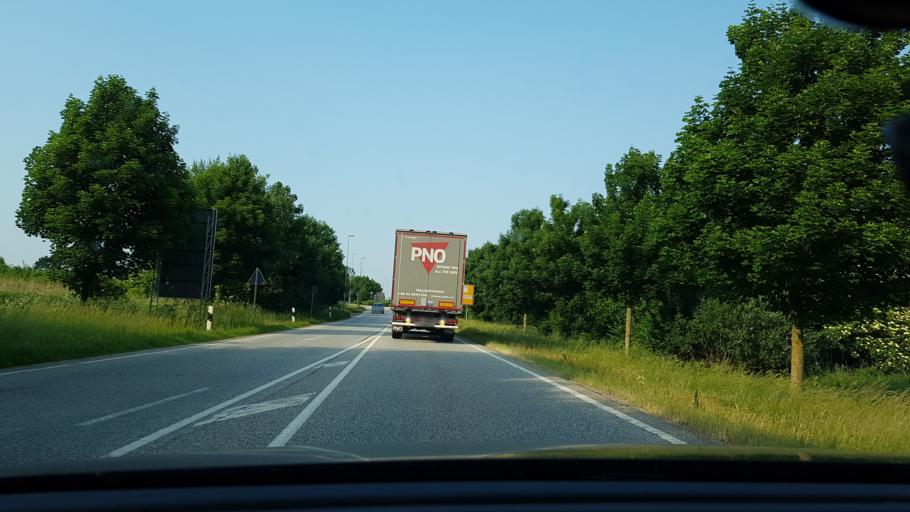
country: DE
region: Schleswig-Holstein
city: Krummesse
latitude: 53.8323
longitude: 10.6486
